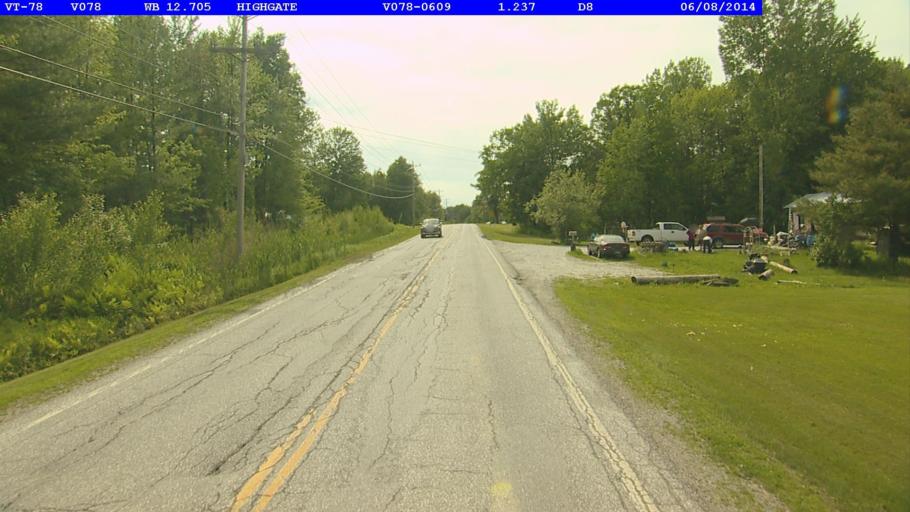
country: US
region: Vermont
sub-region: Franklin County
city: Swanton
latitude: 44.9337
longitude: -73.0766
